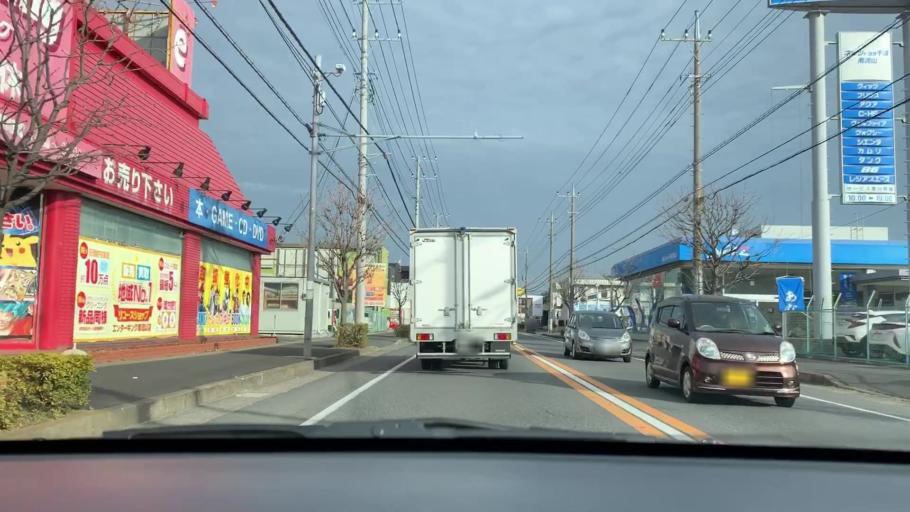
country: JP
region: Chiba
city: Nagareyama
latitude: 35.8383
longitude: 139.8966
